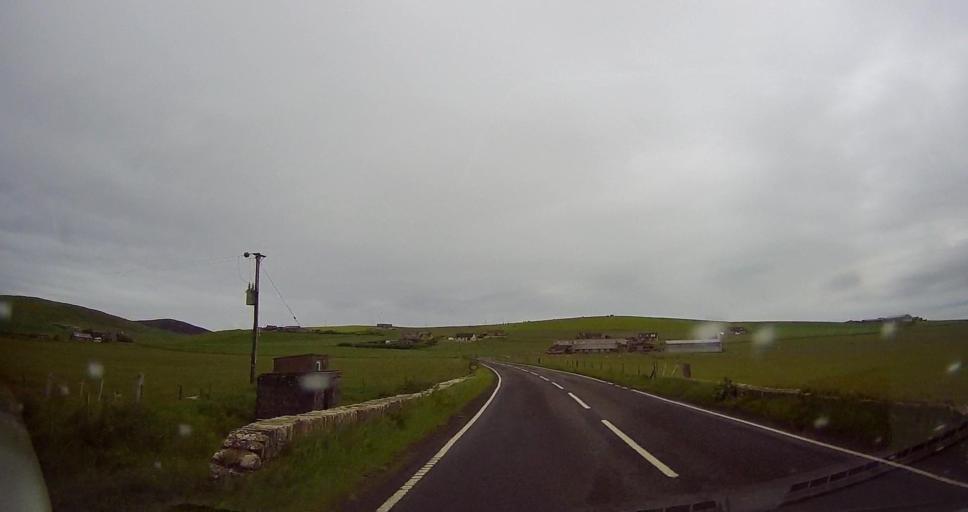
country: GB
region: Scotland
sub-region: Orkney Islands
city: Stromness
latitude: 58.9926
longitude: -3.2911
